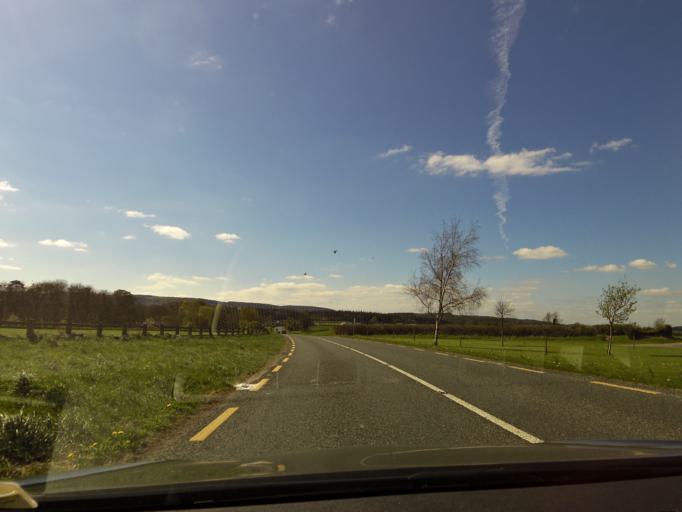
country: IE
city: Ballylinan
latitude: 53.0029
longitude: -7.0589
